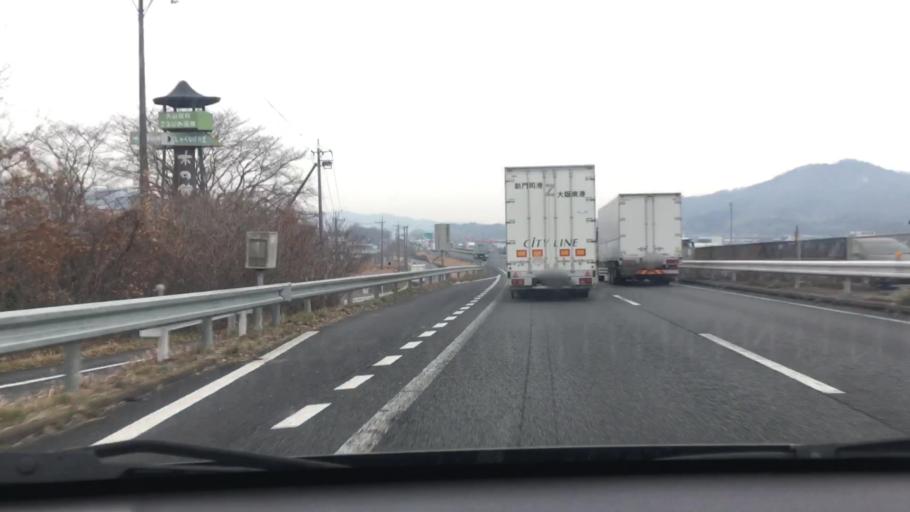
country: JP
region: Mie
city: Ueno-ebisumachi
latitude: 34.7653
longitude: 136.1559
